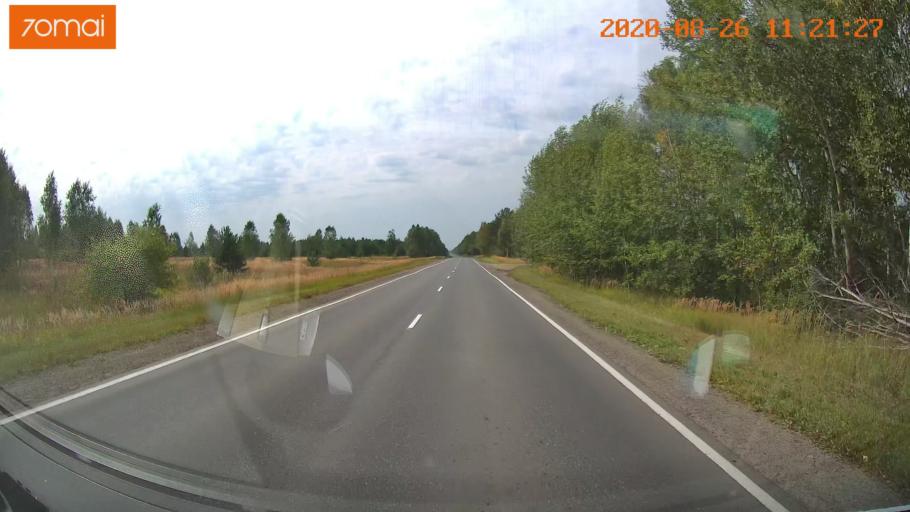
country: RU
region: Rjazan
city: Shilovo
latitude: 54.3761
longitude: 41.0446
